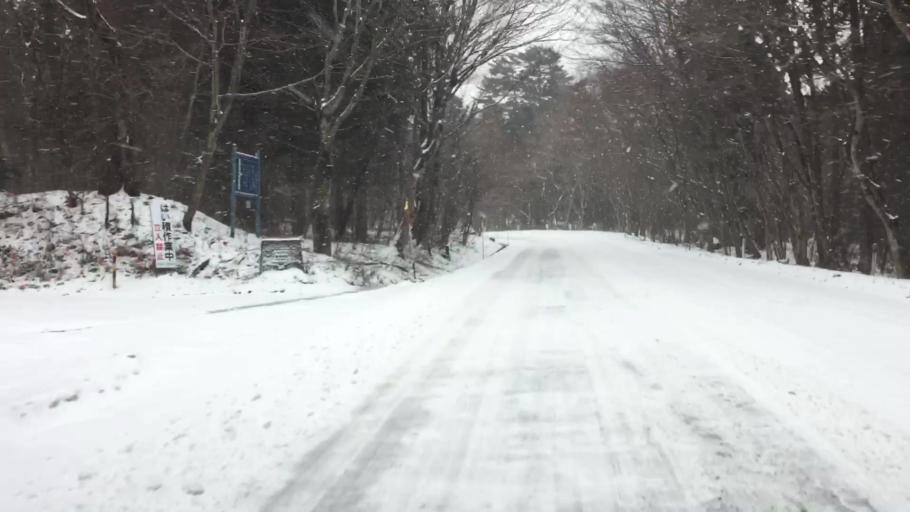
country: JP
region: Tochigi
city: Nikko
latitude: 36.8805
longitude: 139.7223
